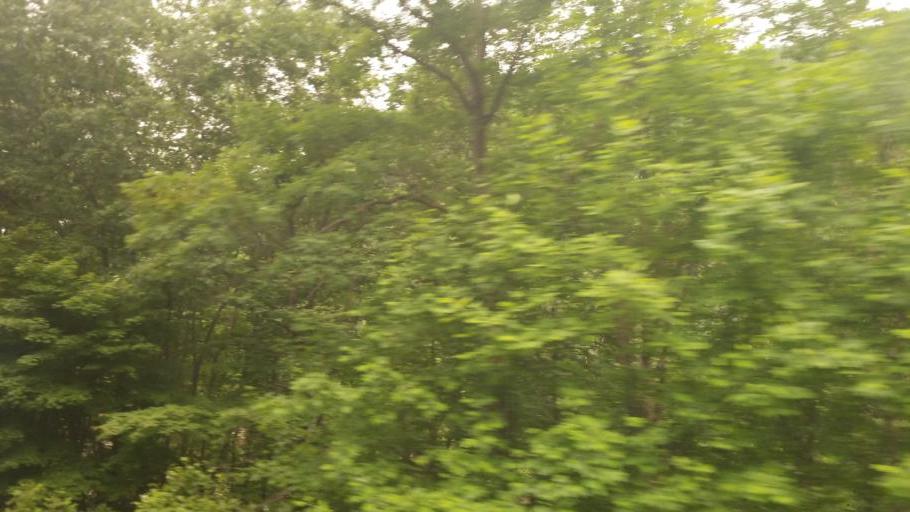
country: US
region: Pennsylvania
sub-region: Fayette County
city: South Connellsville
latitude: 39.8934
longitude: -79.4770
